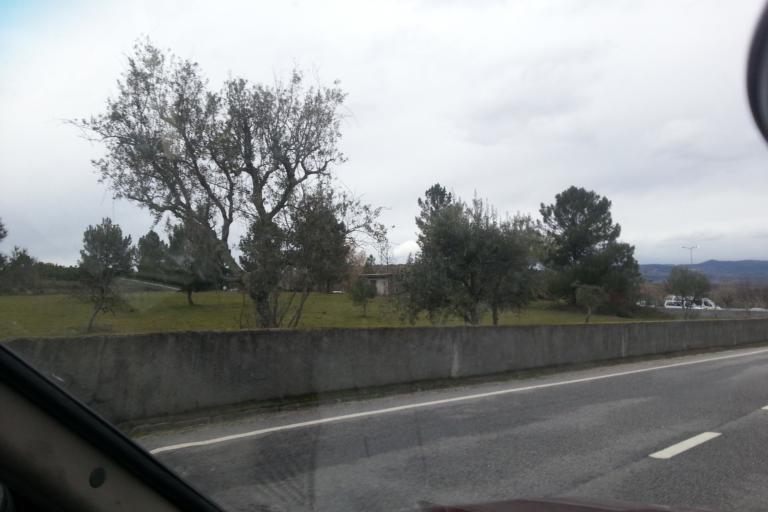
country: PT
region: Guarda
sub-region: Fornos de Algodres
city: Fornos de Algodres
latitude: 40.5290
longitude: -7.5760
